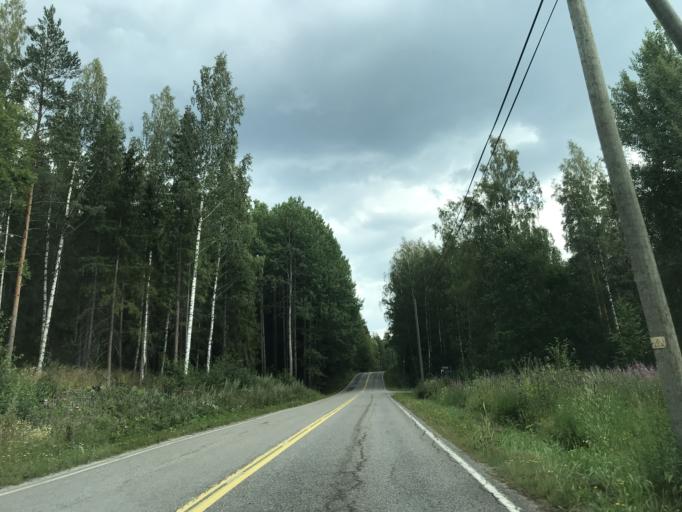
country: FI
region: Uusimaa
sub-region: Helsinki
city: Vihti
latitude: 60.3920
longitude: 24.3333
